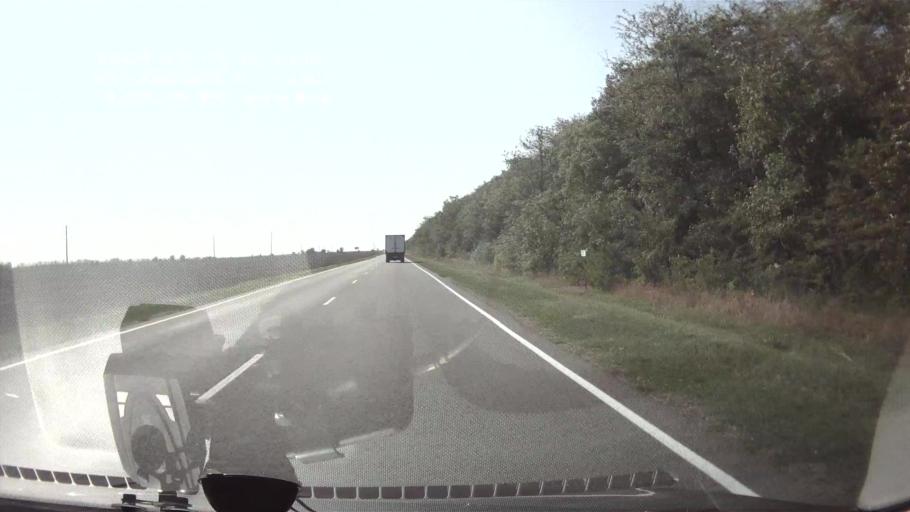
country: RU
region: Krasnodarskiy
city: Novopokrovskaya
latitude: 45.8860
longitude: 40.7209
